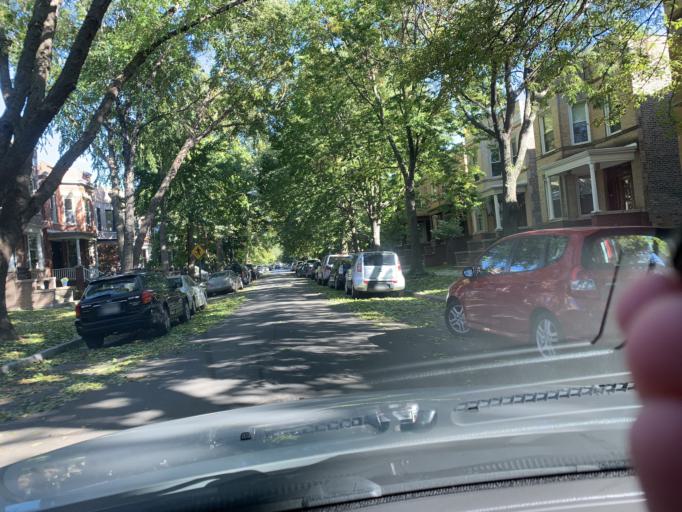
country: US
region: Illinois
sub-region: Cook County
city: Lincolnwood
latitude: 41.9599
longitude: -87.6820
